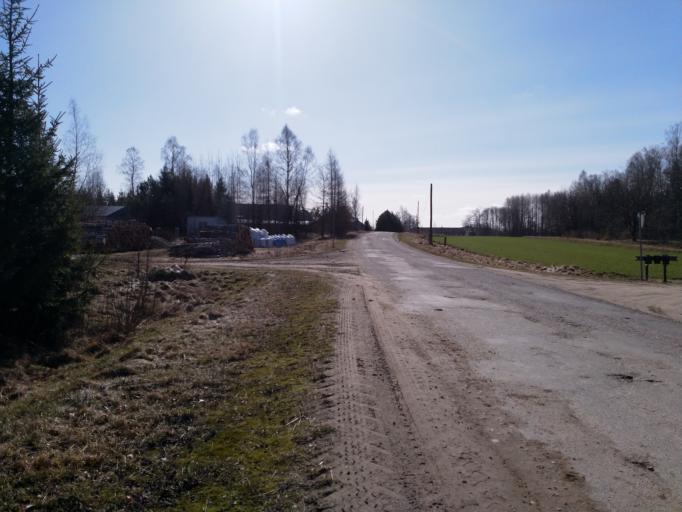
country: LV
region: Aizpute
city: Aizpute
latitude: 56.8305
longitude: 21.7737
